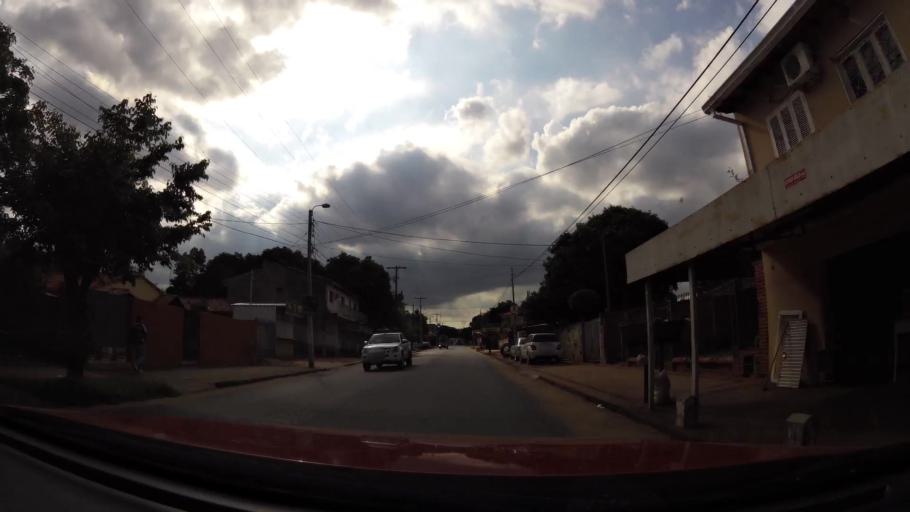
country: PY
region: Central
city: Fernando de la Mora
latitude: -25.3449
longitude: -57.5451
